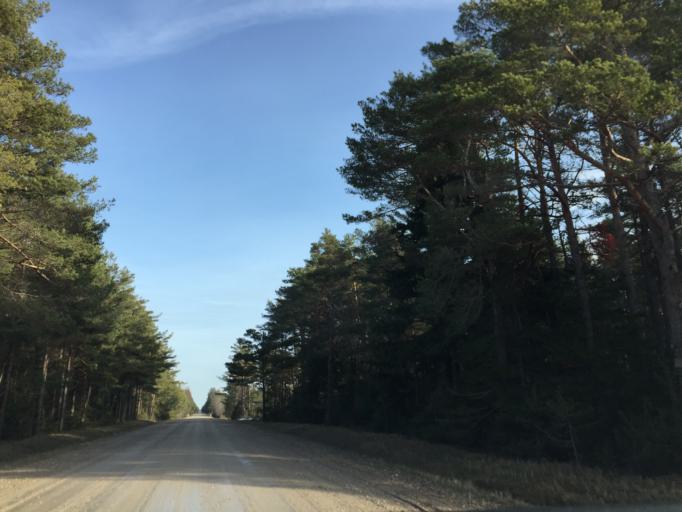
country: EE
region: Saare
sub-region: Kuressaare linn
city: Kuressaare
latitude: 58.3024
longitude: 21.9613
